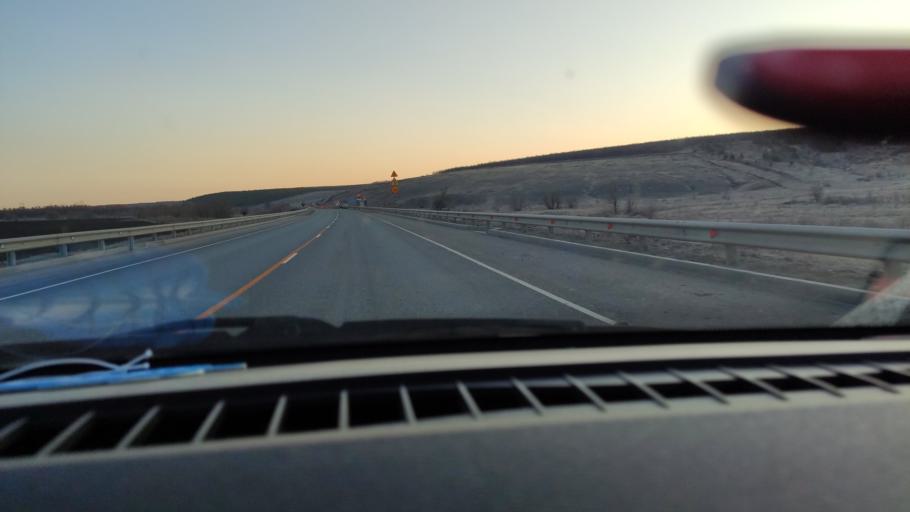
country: RU
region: Saratov
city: Yelshanka
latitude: 51.8656
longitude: 46.5015
